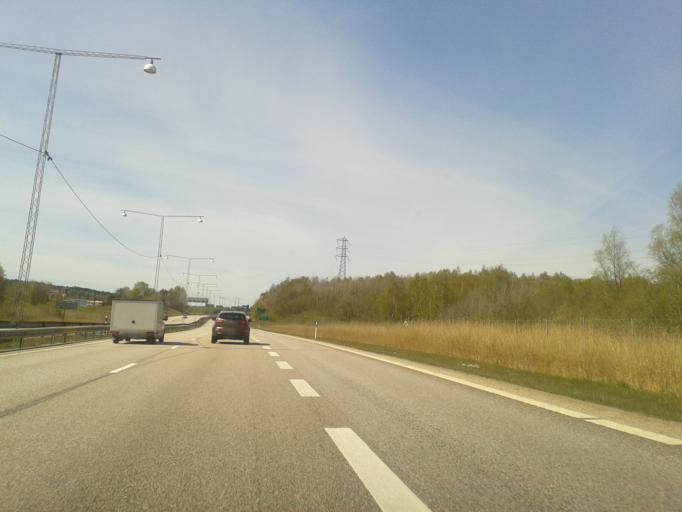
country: SE
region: Vaestra Goetaland
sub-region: Kungalvs Kommun
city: Kungalv
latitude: 57.8787
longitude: 11.9575
